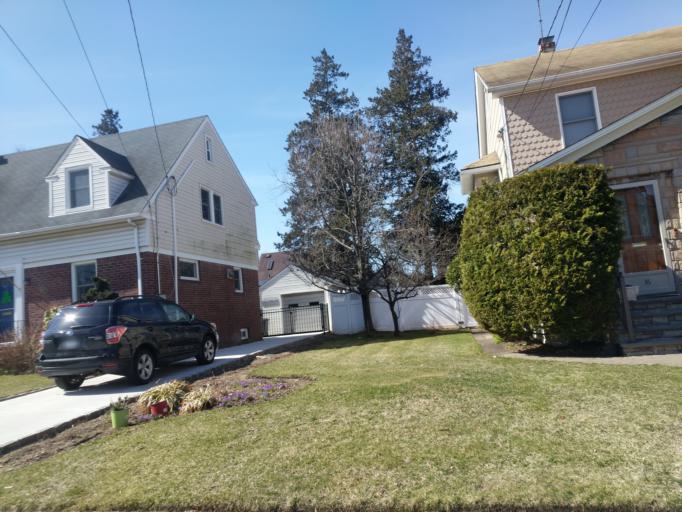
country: US
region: New York
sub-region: Nassau County
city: Lynbrook
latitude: 40.6521
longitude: -73.6772
